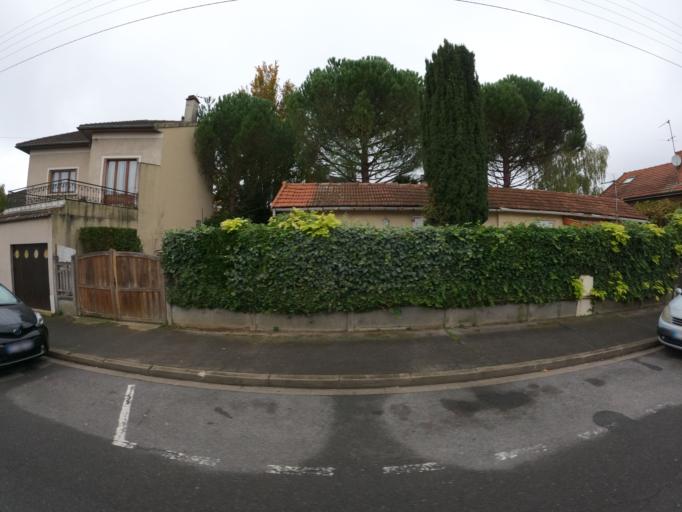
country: FR
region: Ile-de-France
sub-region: Departement du Val-de-Marne
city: Ormesson-sur-Marne
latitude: 48.7884
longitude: 2.5399
